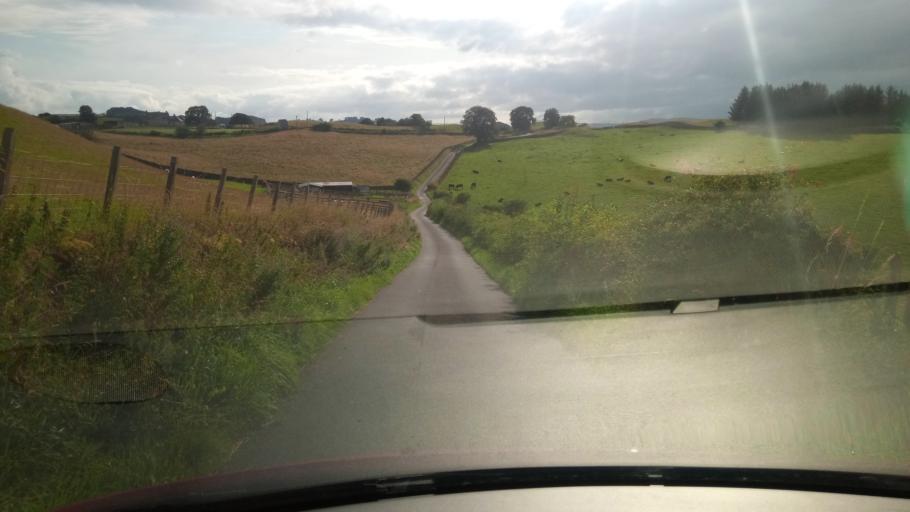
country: GB
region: Scotland
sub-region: The Scottish Borders
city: Hawick
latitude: 55.4239
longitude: -2.7707
